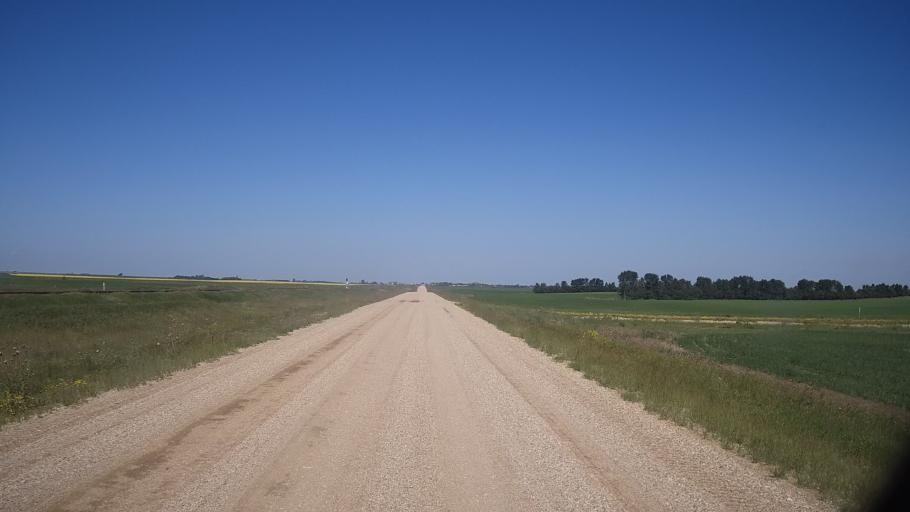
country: CA
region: Saskatchewan
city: Watrous
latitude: 51.8751
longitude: -106.0054
